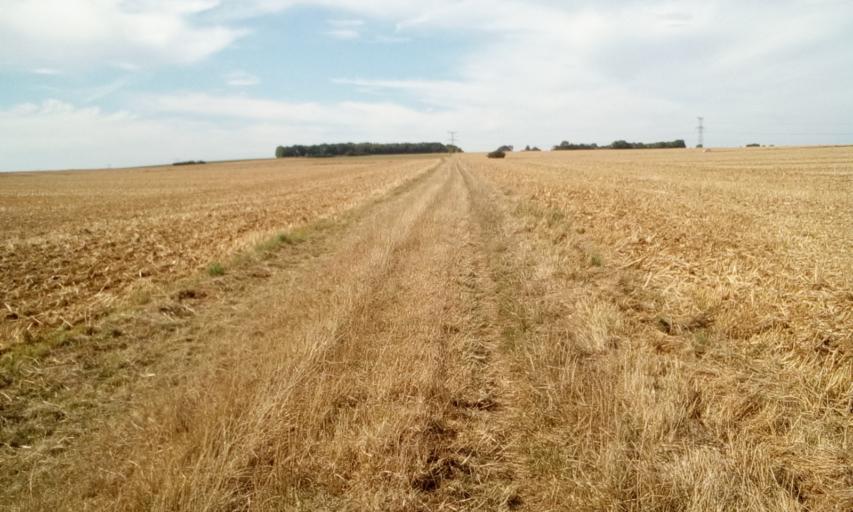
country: FR
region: Lower Normandy
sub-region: Departement du Calvados
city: Fontaine-Etoupefour
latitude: 49.1116
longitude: -0.4480
